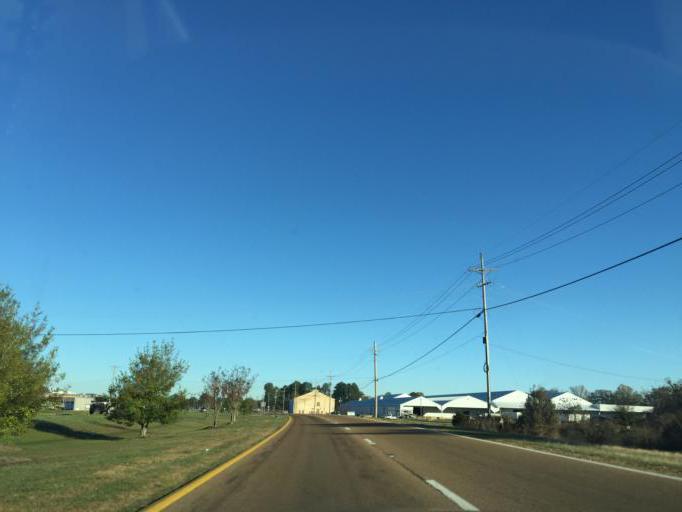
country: US
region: Mississippi
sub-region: Rankin County
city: Flowood
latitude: 32.3023
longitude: -90.1415
